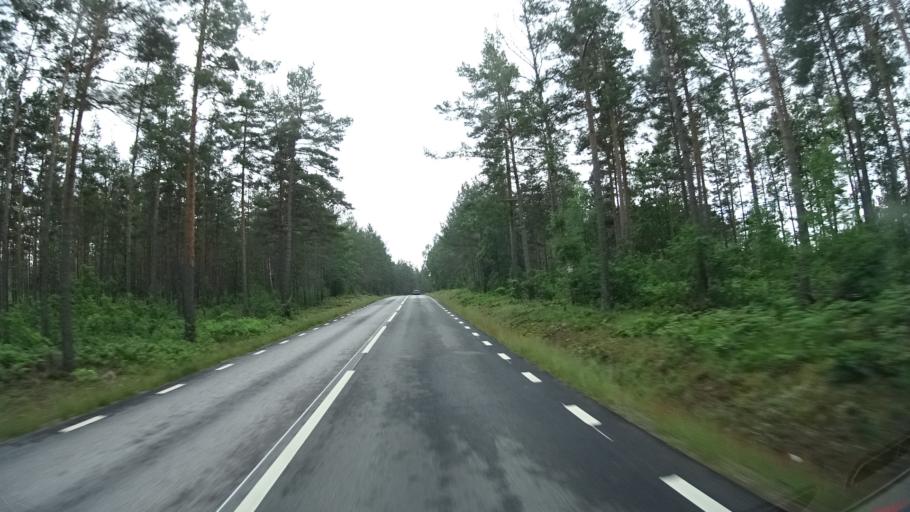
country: SE
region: Kalmar
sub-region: Oskarshamns Kommun
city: Oskarshamn
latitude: 57.3261
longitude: 16.2667
